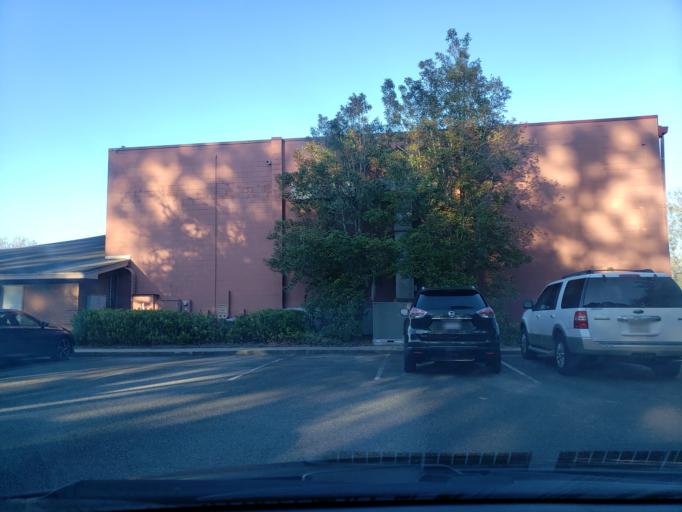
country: US
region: Georgia
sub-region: Chatham County
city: Montgomery
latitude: 31.9965
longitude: -81.1479
